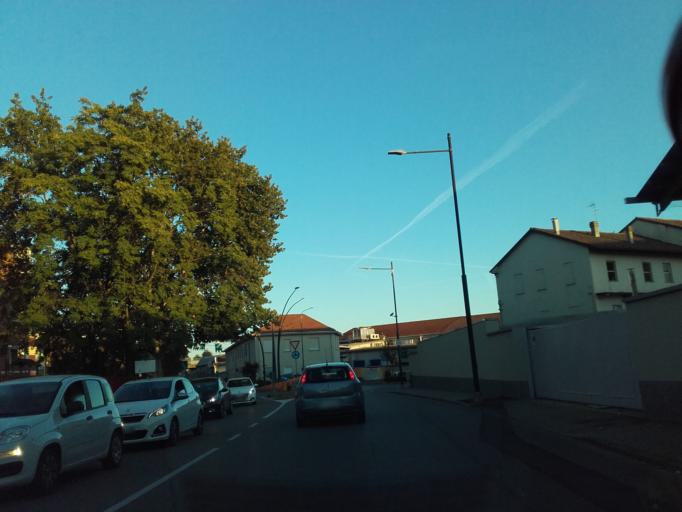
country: IT
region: Piedmont
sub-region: Provincia di Asti
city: Asti
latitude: 44.8942
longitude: 8.1973
